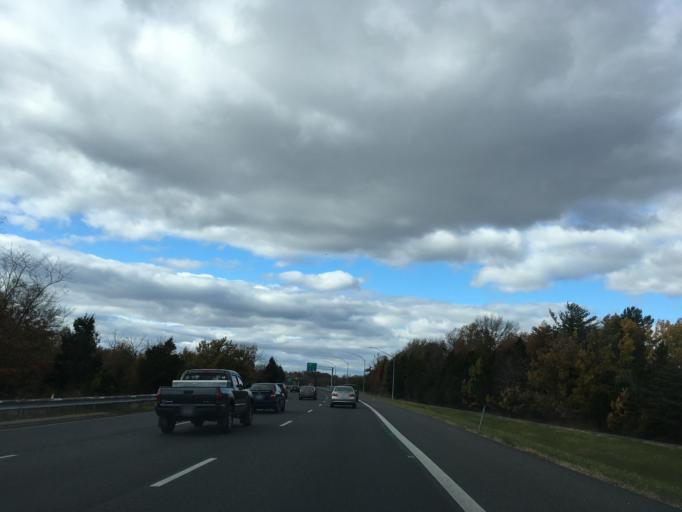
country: US
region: Maryland
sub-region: Anne Arundel County
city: Jessup
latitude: 39.1803
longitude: -76.7908
